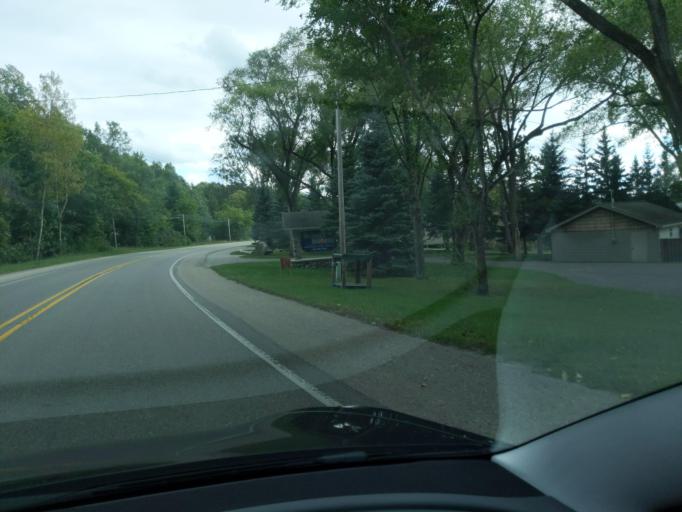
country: US
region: Michigan
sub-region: Kalkaska County
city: Rapid City
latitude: 44.8722
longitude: -85.2781
